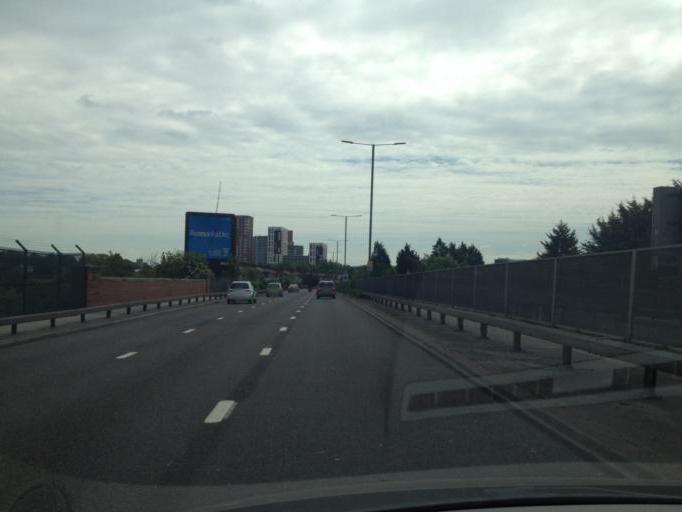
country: GB
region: England
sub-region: Greater London
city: Acton
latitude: 51.5253
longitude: -0.2704
